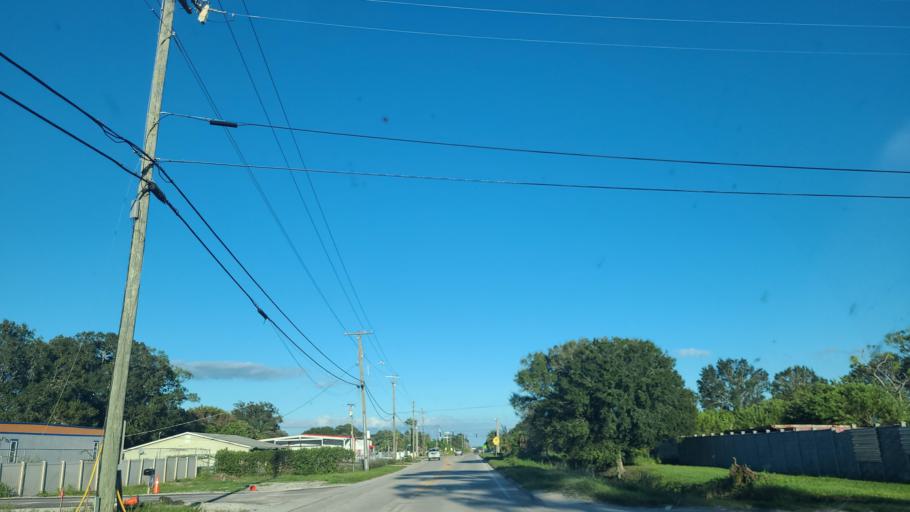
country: US
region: Florida
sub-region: Indian River County
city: Gifford
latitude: 27.6752
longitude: -80.4319
